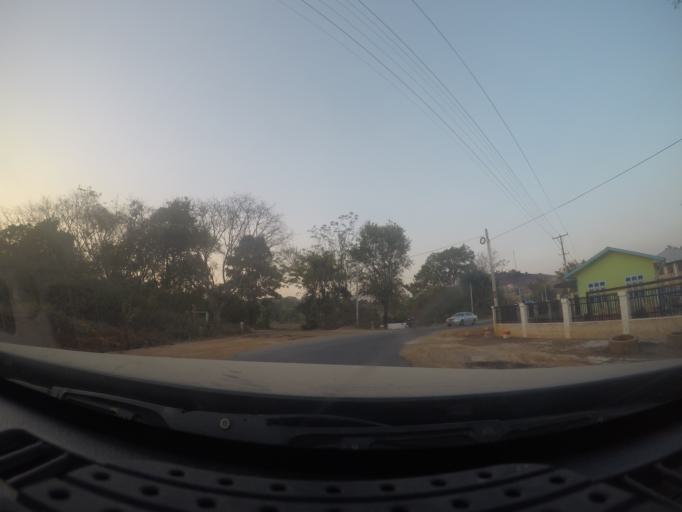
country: MM
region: Shan
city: Taunggyi
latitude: 20.6910
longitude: 97.0601
